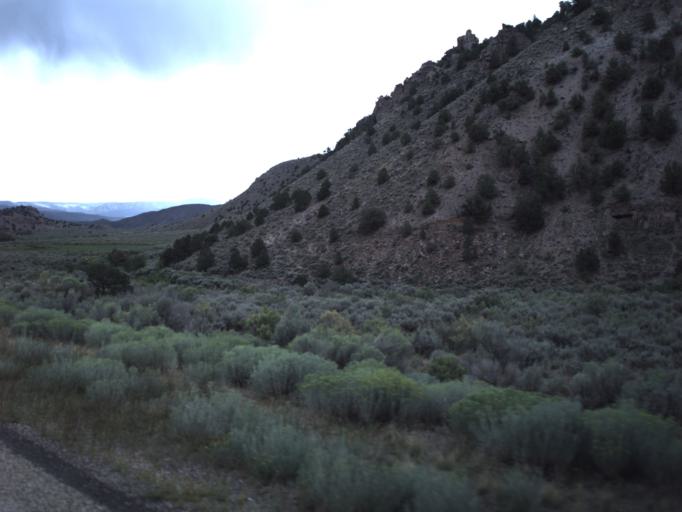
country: US
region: Utah
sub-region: Piute County
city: Junction
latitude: 38.1890
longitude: -112.0982
